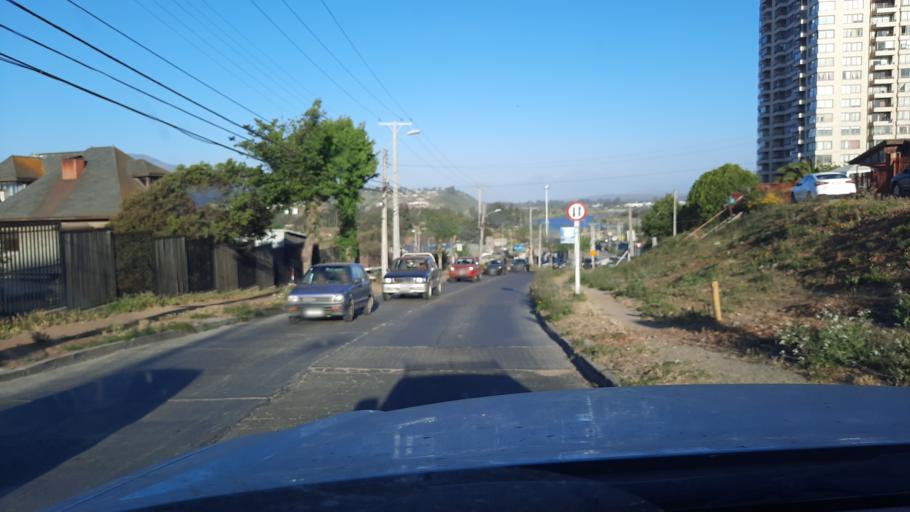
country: CL
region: Valparaiso
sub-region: Provincia de Valparaiso
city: Vina del Mar
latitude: -32.9214
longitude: -71.5097
